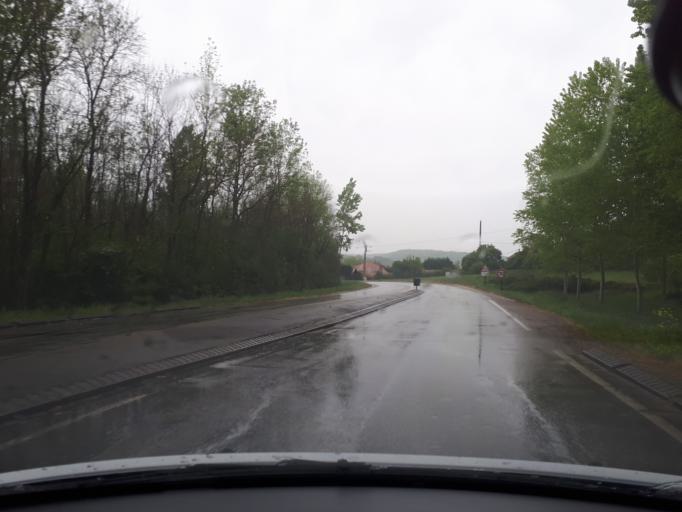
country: FR
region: Rhone-Alpes
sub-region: Departement de l'Isere
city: L'Isle-d'Abeau
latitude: 45.6362
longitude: 5.2396
